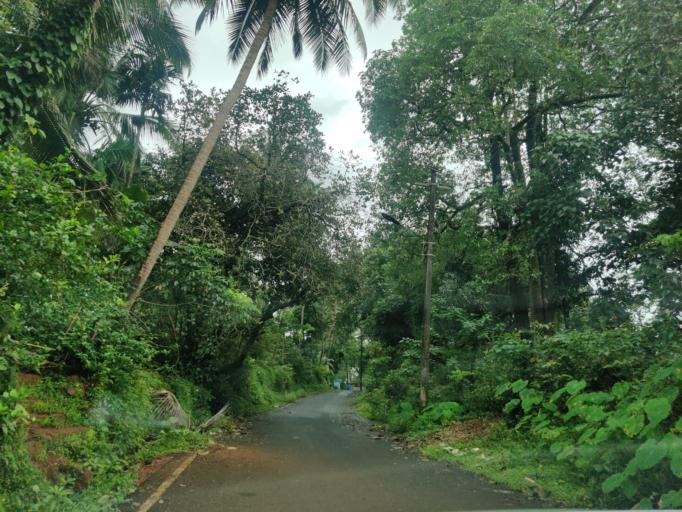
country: IN
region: Goa
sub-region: North Goa
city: Valpoy
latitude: 15.5307
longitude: 74.1384
